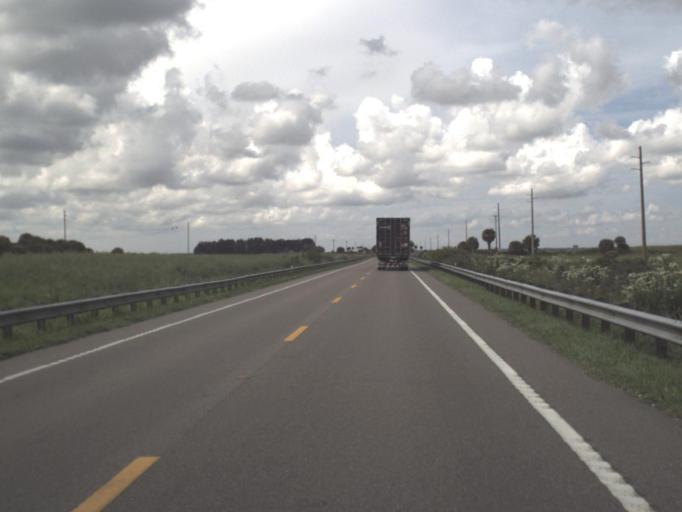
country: US
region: Florida
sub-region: Highlands County
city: Lake Placid
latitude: 27.2092
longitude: -81.1973
